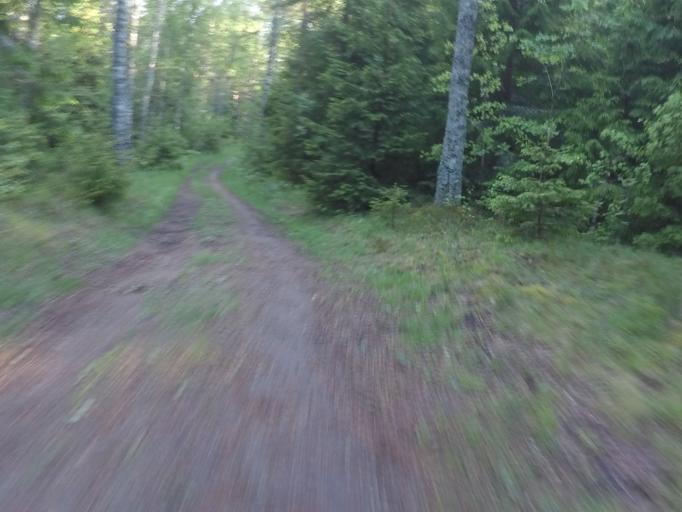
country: SE
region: Soedermanland
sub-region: Eskilstuna Kommun
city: Hallbybrunn
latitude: 59.3964
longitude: 16.3957
